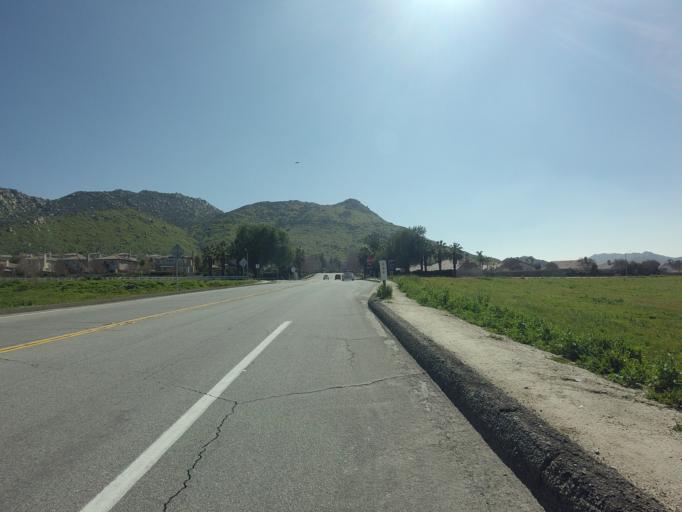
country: US
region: California
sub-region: Riverside County
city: Moreno Valley
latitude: 33.9109
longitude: -117.1567
